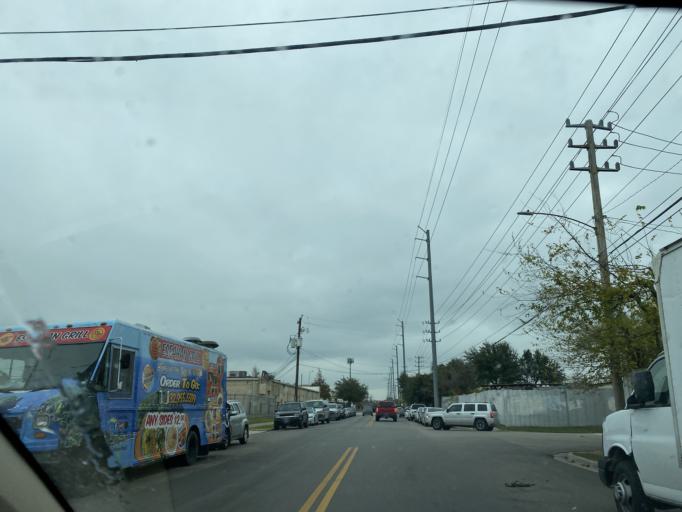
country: US
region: Texas
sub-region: Harris County
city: Piney Point Village
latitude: 29.7278
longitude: -95.5196
